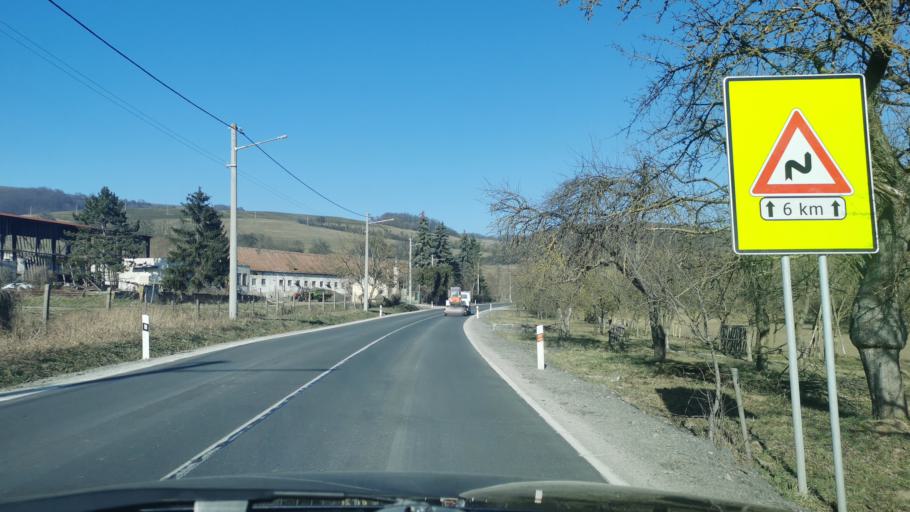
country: SK
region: Trnavsky
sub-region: Okres Senica
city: Senica
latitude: 48.7411
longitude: 17.4384
